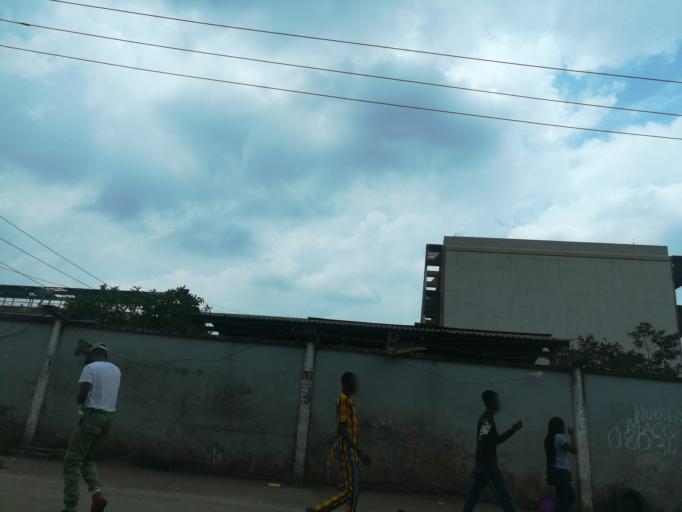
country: NG
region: Lagos
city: Ojota
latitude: 6.5885
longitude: 3.3787
